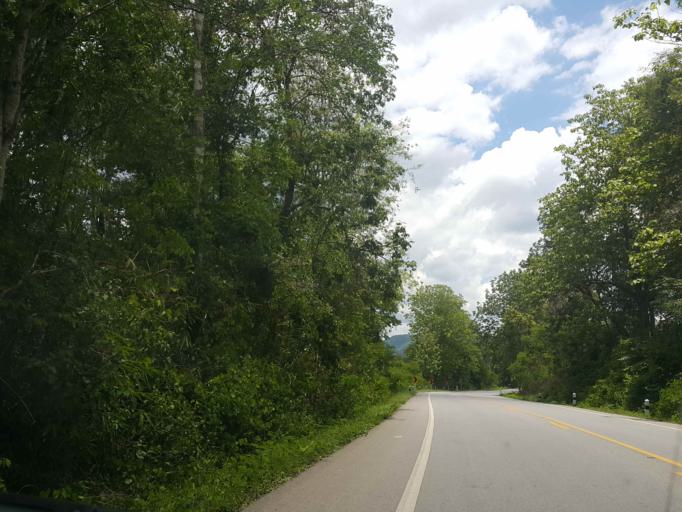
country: TH
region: Nan
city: Wiang Sa
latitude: 18.5186
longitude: 100.5883
